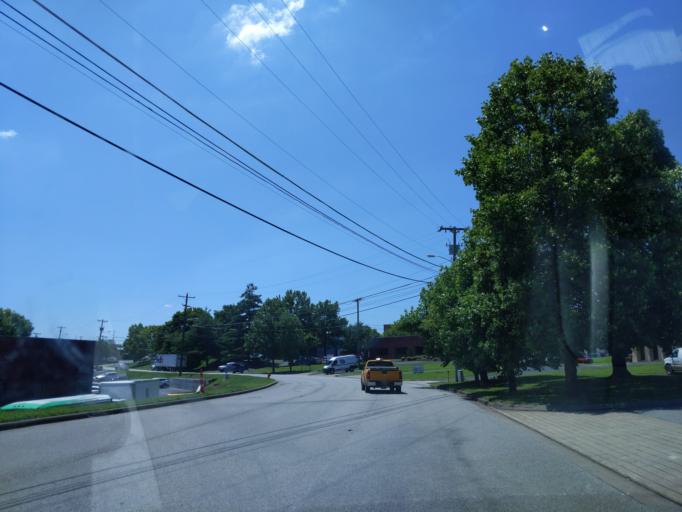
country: US
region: Tennessee
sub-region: Davidson County
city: Nashville
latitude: 36.1485
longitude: -86.7421
